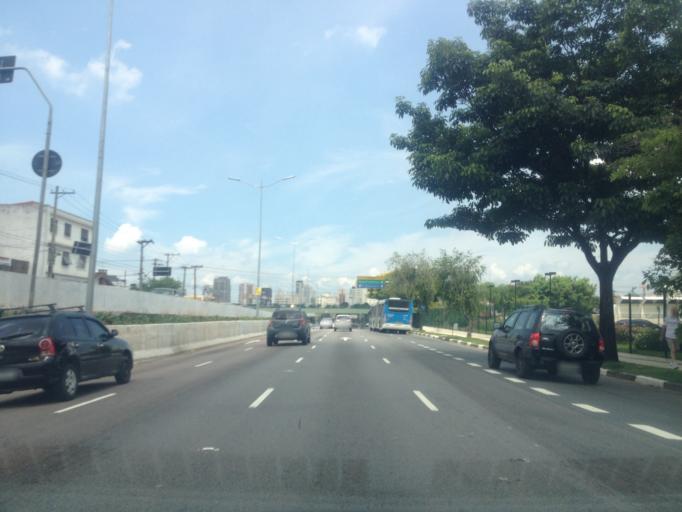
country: BR
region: Sao Paulo
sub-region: Sao Paulo
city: Sao Paulo
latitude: -23.6149
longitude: -46.6595
